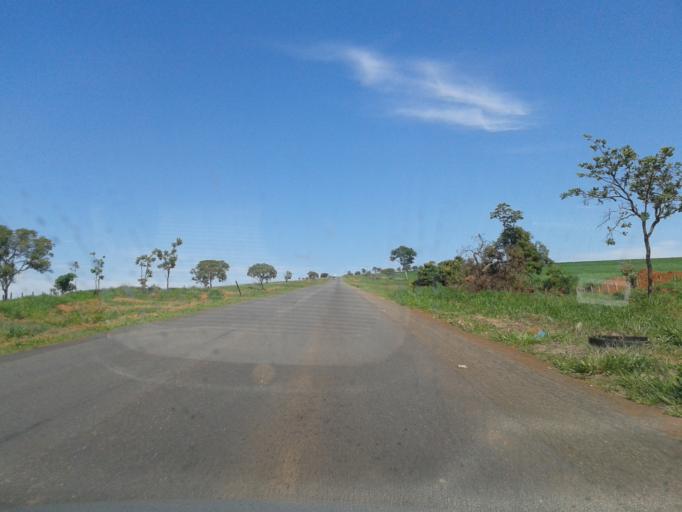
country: BR
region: Goias
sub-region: Bela Vista De Goias
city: Bela Vista de Goias
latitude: -17.1608
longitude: -48.7850
